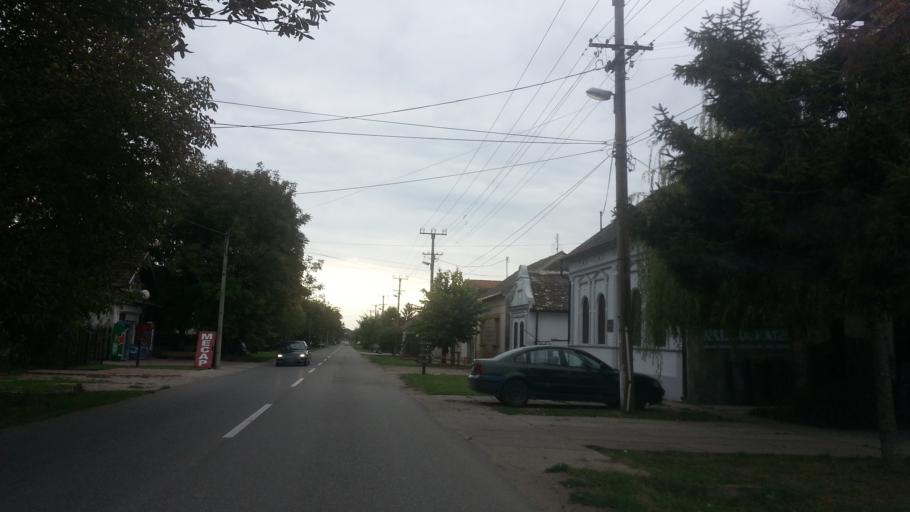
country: RS
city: Stari Banovci
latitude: 44.9904
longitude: 20.2886
